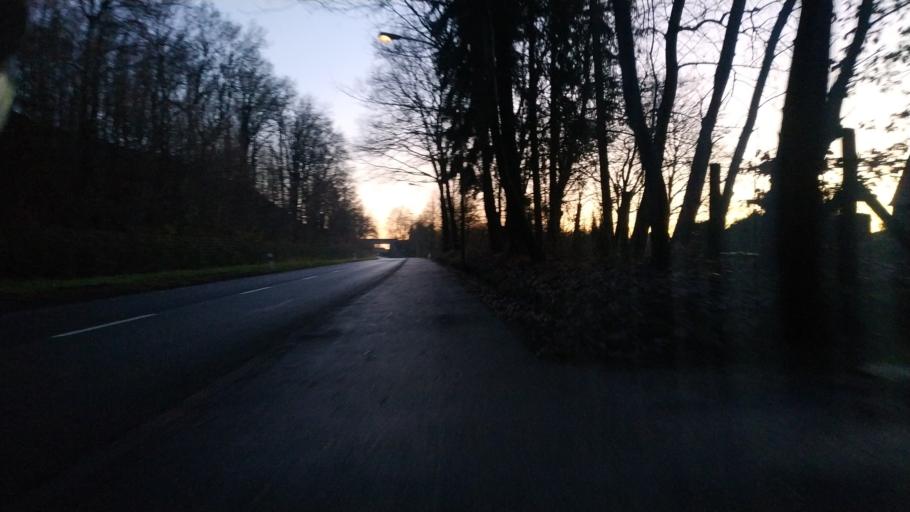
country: DE
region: North Rhine-Westphalia
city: Ibbenburen
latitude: 52.2907
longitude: 7.7337
